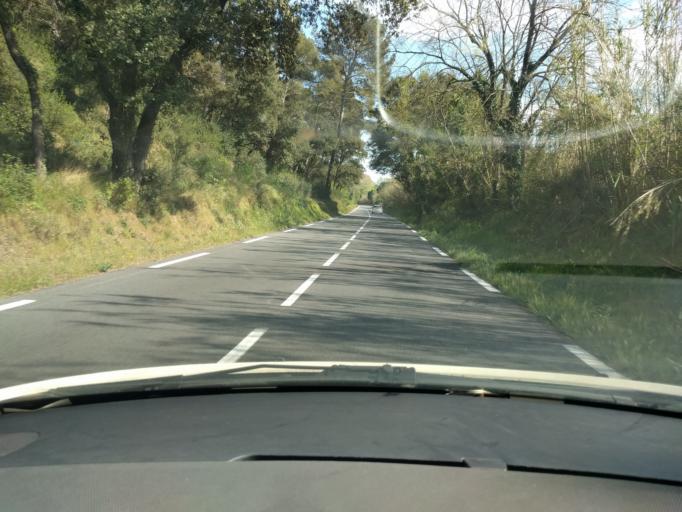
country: FR
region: Provence-Alpes-Cote d'Azur
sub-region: Departement du Var
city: Hyeres
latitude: 43.1643
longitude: 6.1208
